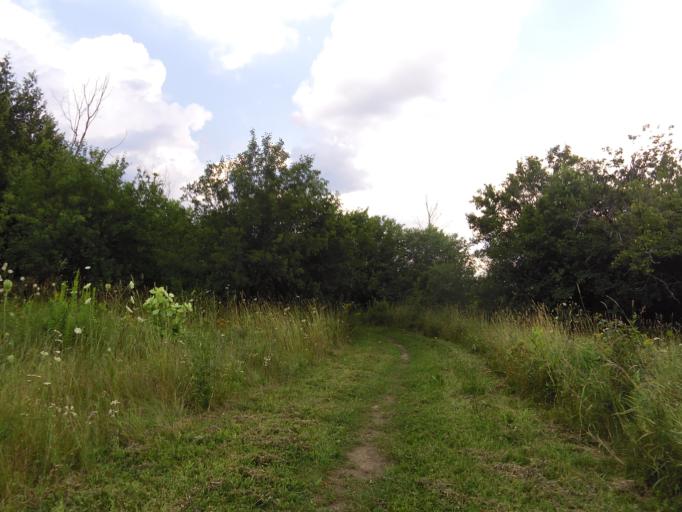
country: CA
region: Ontario
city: Bells Corners
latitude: 45.3137
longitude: -75.8087
